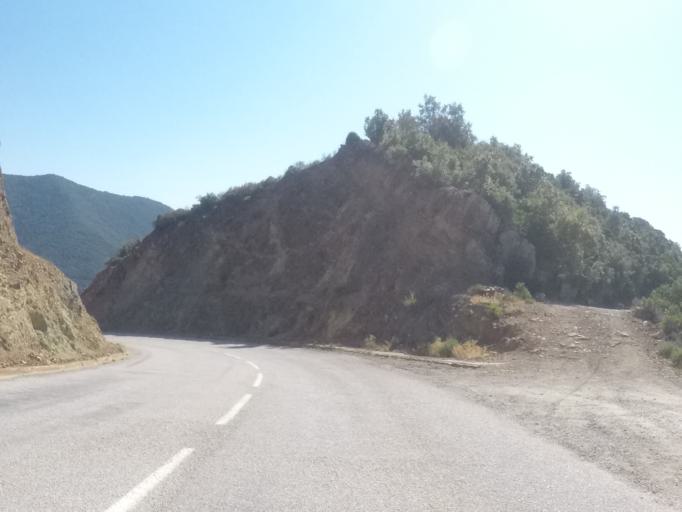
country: FR
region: Corsica
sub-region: Departement de la Corse-du-Sud
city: Cargese
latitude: 42.3520
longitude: 8.6440
